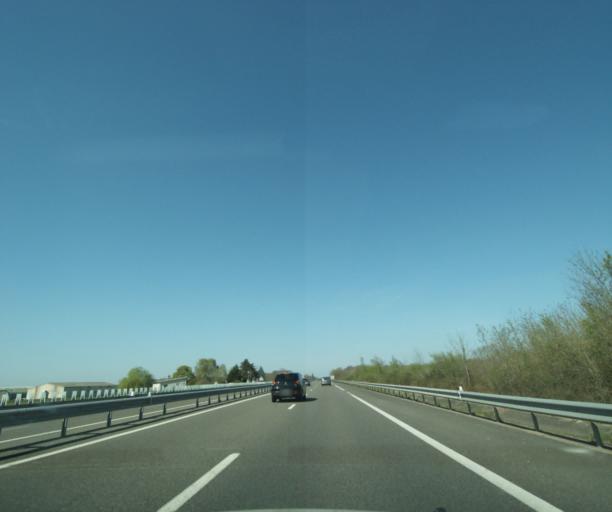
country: FR
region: Bourgogne
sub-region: Departement de la Nievre
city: Cosne-Cours-sur-Loire
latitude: 47.3588
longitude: 2.9236
